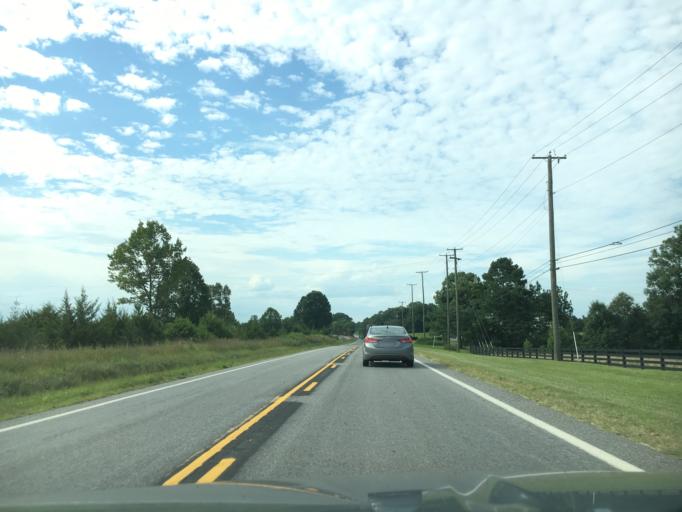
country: US
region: Virginia
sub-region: Campbell County
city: Brookneal
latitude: 37.0800
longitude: -78.9857
